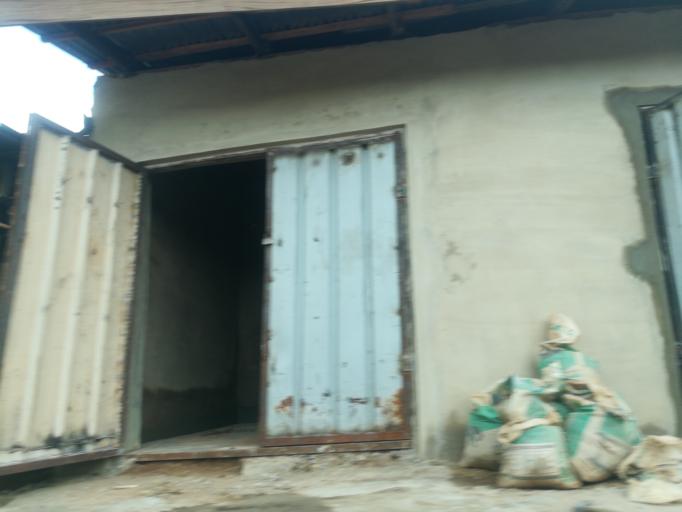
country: NG
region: Oyo
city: Ibadan
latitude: 7.3898
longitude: 3.8845
